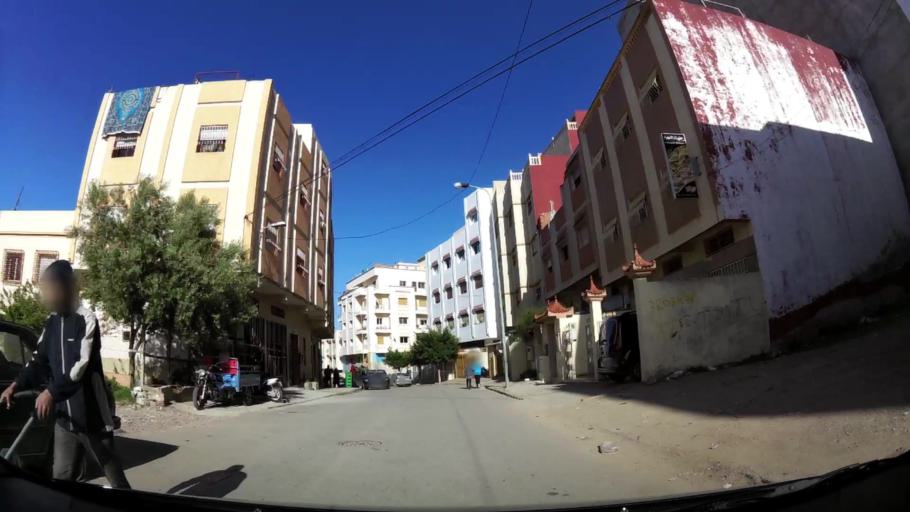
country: MA
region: Tanger-Tetouan
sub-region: Tanger-Assilah
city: Tangier
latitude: 35.7422
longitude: -5.8044
